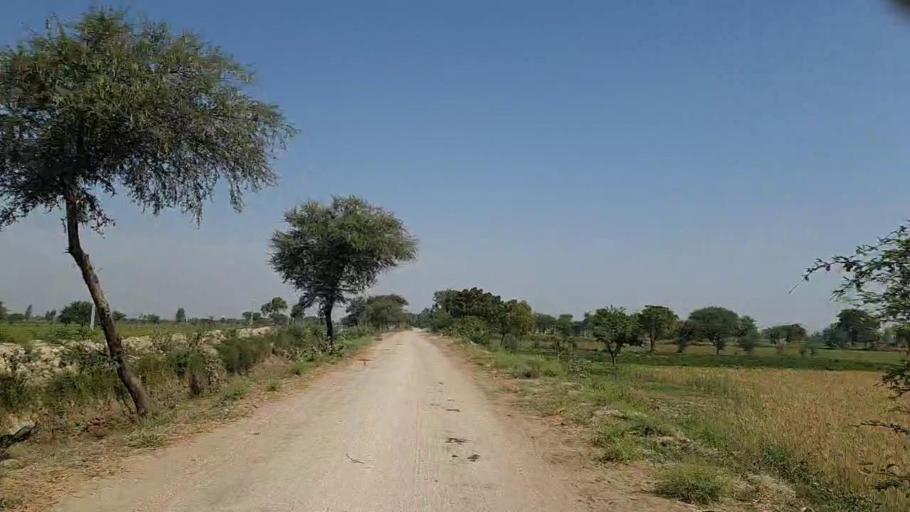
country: PK
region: Sindh
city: Mirpur Batoro
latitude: 24.6961
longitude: 68.2573
